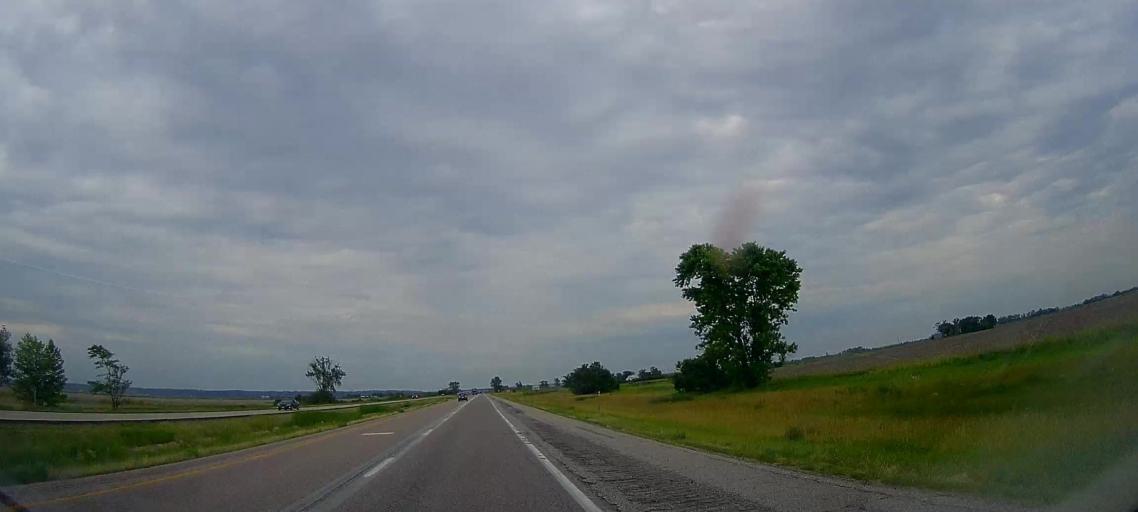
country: US
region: Iowa
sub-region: Harrison County
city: Missouri Valley
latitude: 41.6105
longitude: -95.9760
